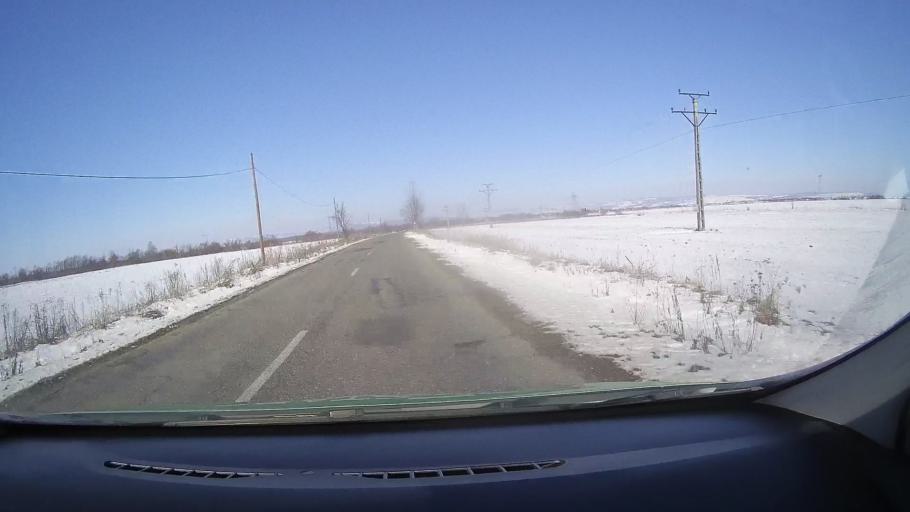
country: RO
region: Brasov
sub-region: Comuna Harseni
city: Harseni
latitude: 45.7699
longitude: 25.0024
